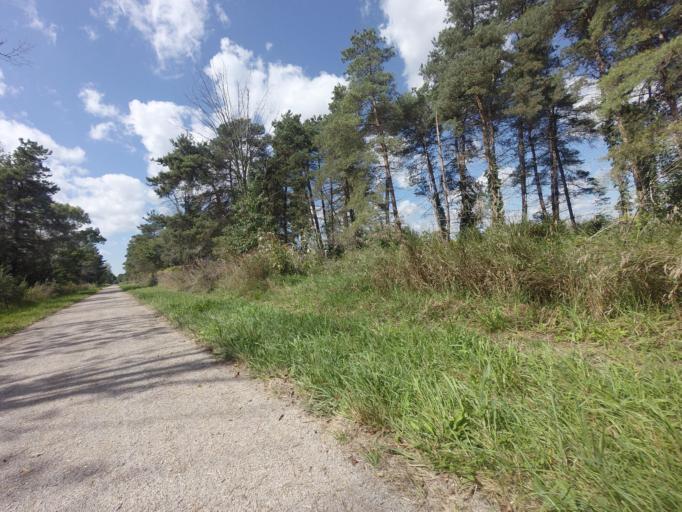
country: CA
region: Ontario
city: Huron East
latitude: 43.6827
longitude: -81.3055
